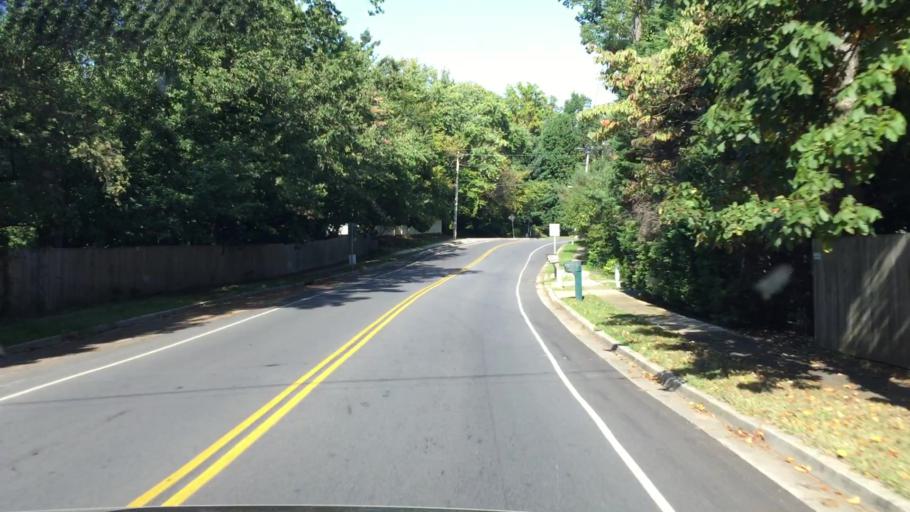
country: US
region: Maryland
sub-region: Anne Arundel County
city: Arnold
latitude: 39.0489
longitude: -76.4816
